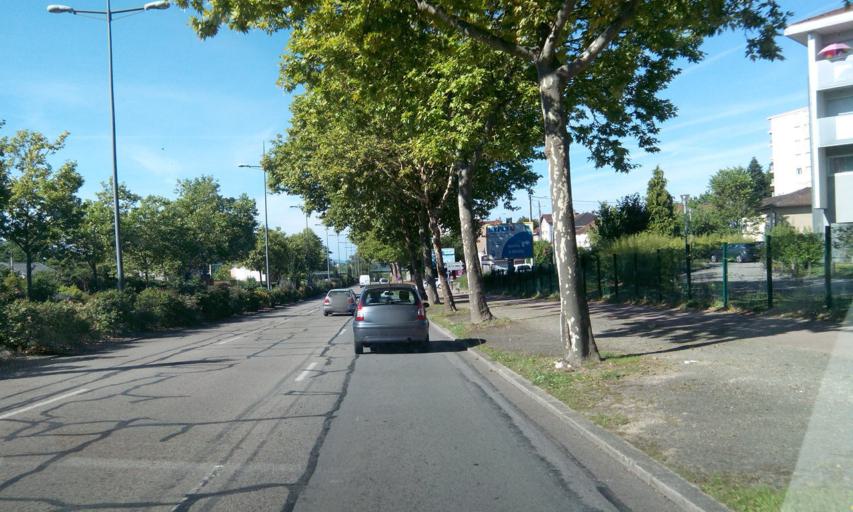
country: FR
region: Limousin
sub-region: Departement de la Haute-Vienne
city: Limoges
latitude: 45.8430
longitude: 1.2387
